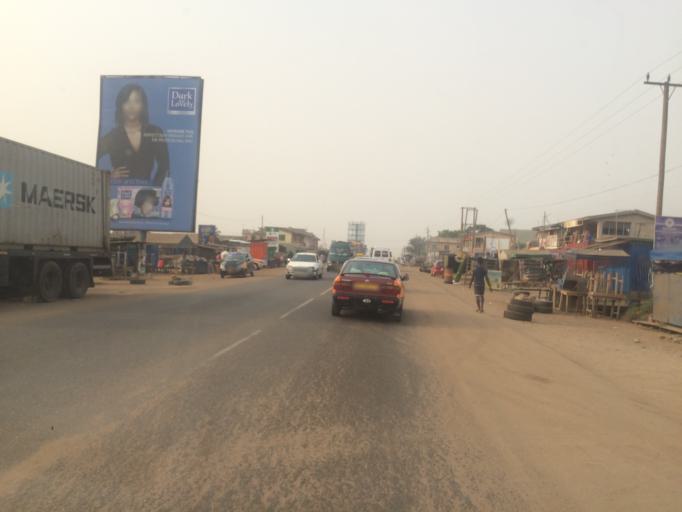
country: GH
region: Greater Accra
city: Nungua
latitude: 5.6046
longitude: -0.0783
